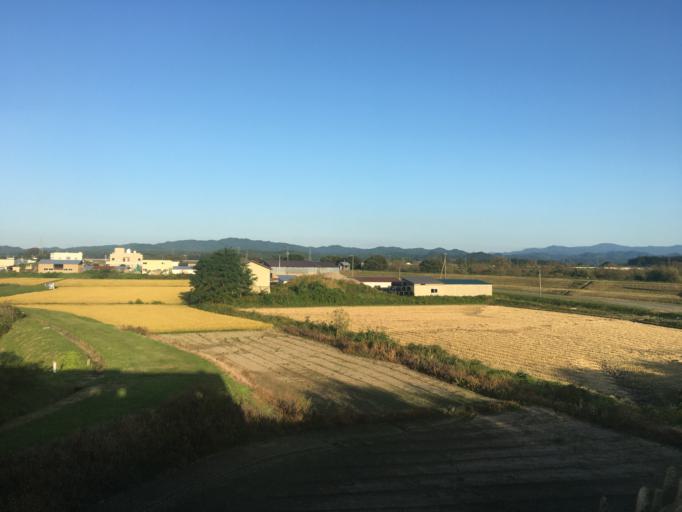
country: JP
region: Akita
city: Takanosu
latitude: 40.2154
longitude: 140.3546
